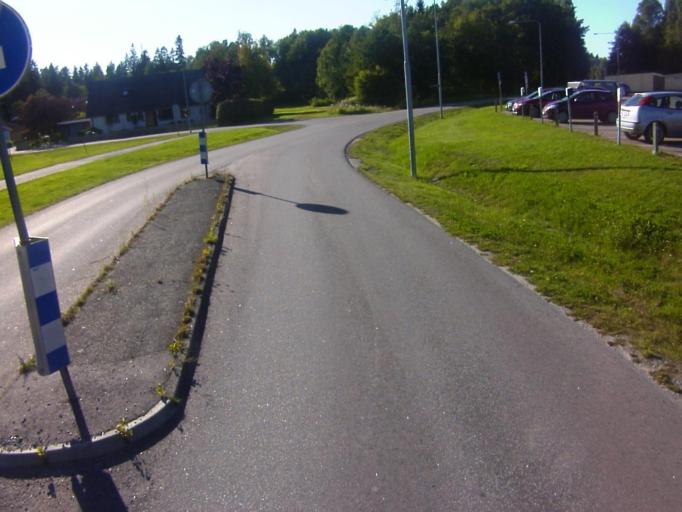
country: SE
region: Soedermanland
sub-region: Eskilstuna Kommun
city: Hallbybrunn
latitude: 59.3892
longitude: 16.4140
